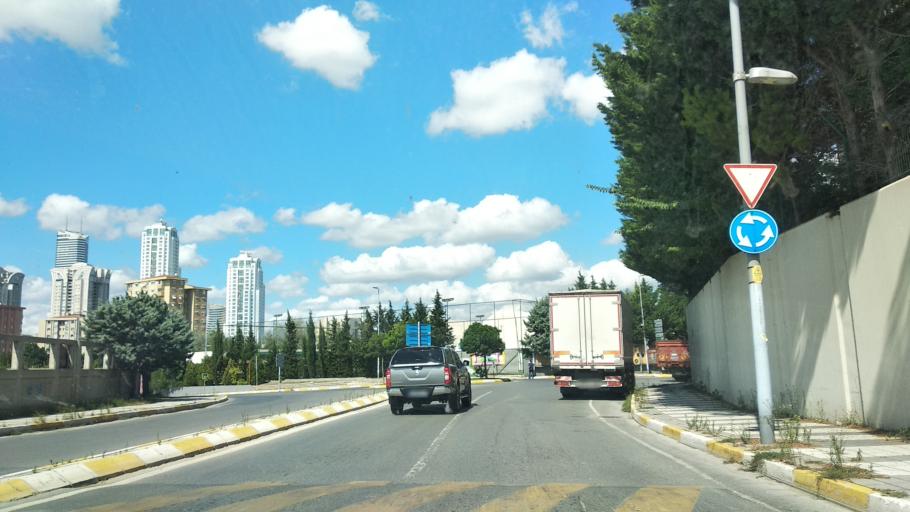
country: TR
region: Istanbul
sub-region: Atasehir
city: Atasehir
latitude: 40.9838
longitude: 29.1290
